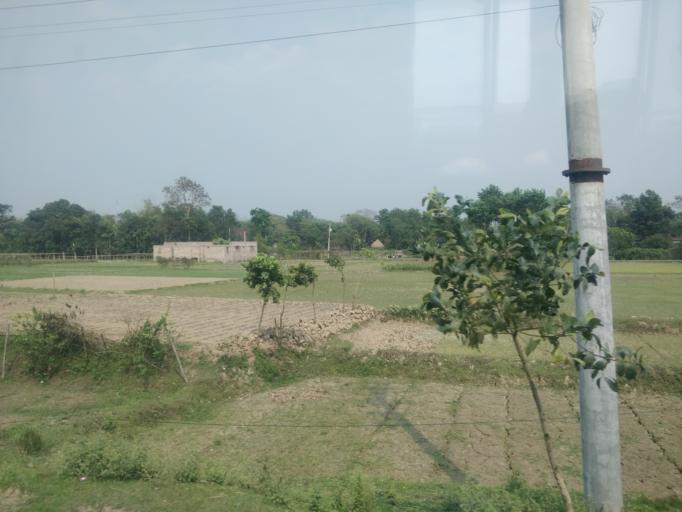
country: BD
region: Sylhet
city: Habiganj
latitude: 24.3245
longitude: 91.4334
